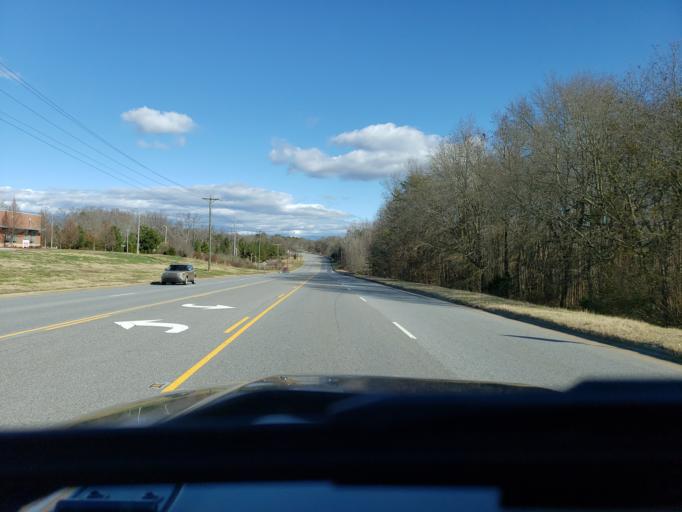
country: US
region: North Carolina
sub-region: Cleveland County
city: Shelby
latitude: 35.2631
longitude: -81.5503
